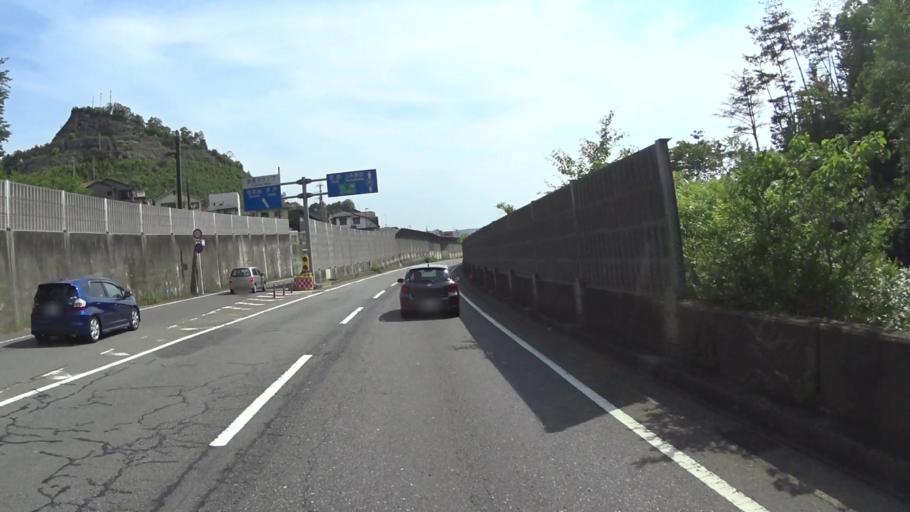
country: JP
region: Shiga Prefecture
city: Otsu-shi
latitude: 34.9985
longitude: 135.8368
